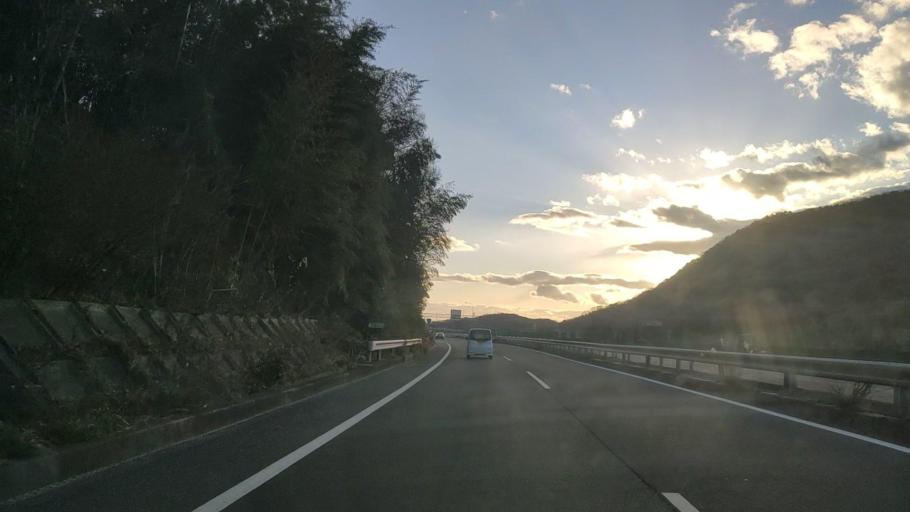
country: JP
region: Hyogo
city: Tatsunocho-tominaga
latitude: 34.8552
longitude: 134.6071
